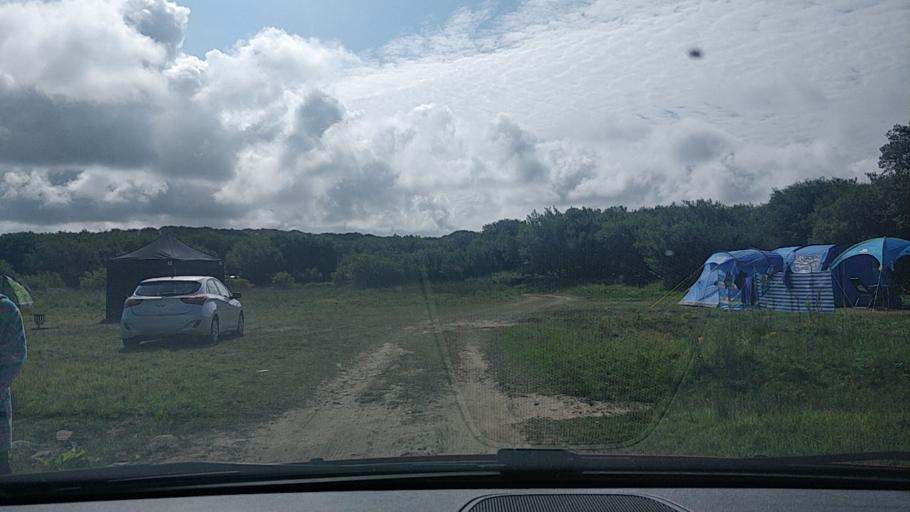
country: GB
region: Wales
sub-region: Gwynedd
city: Llanfair
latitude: 52.8104
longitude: -4.1443
